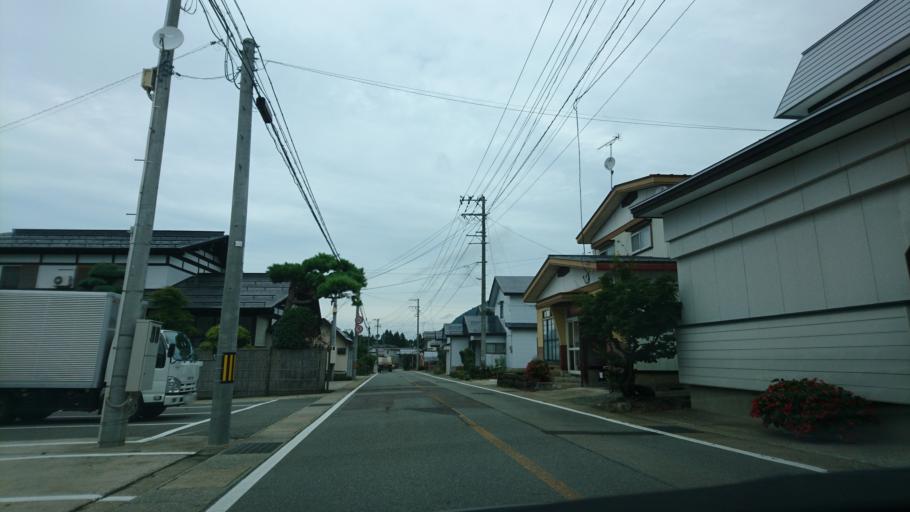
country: JP
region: Akita
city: Yuzawa
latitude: 39.1080
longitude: 140.5828
